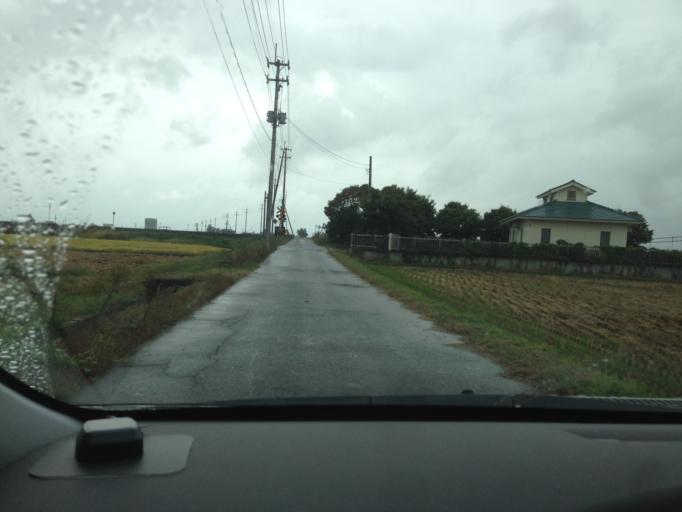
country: JP
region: Fukushima
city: Kitakata
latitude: 37.4644
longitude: 139.8649
